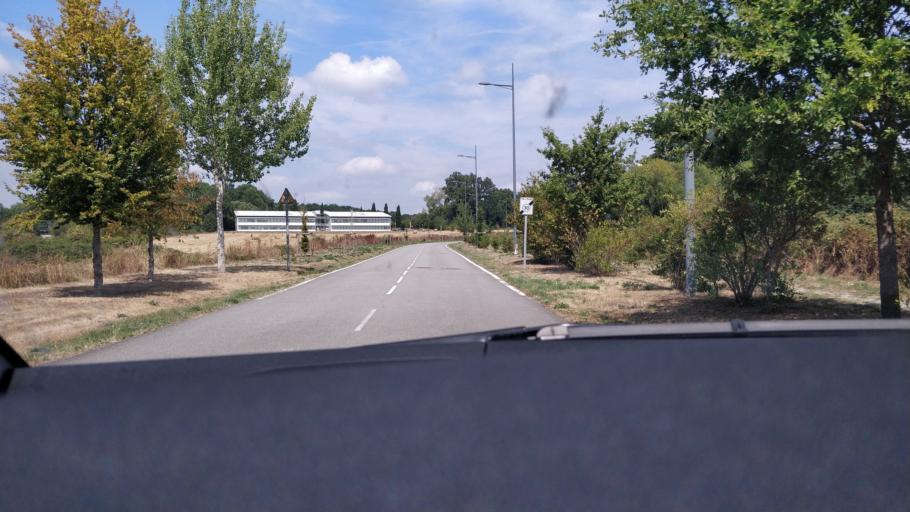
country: FR
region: Limousin
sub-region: Departement de la Haute-Vienne
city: Le Palais-sur-Vienne
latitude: 45.8592
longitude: 1.2989
